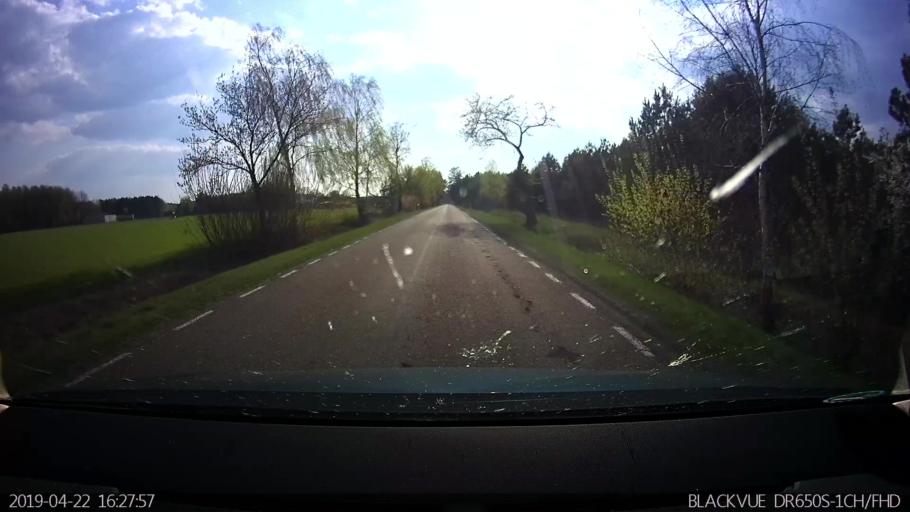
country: PL
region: Podlasie
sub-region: Powiat siemiatycki
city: Milejczyce
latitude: 52.5421
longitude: 23.1902
